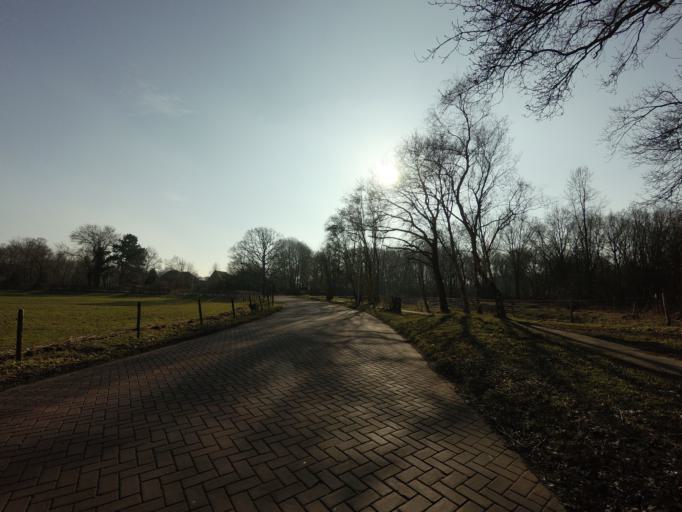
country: NL
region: North Holland
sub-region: Gemeente Bloemendaal
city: Bloemendaal
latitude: 52.4296
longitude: 4.6258
